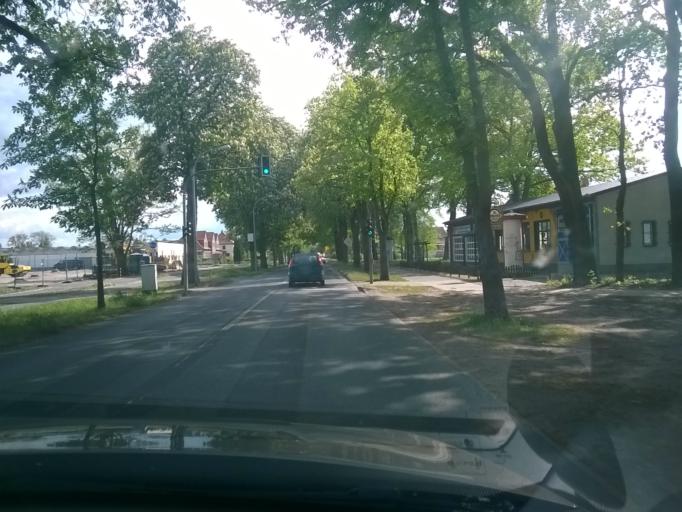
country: DE
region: Brandenburg
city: Wittstock
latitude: 53.1714
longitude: 12.4973
